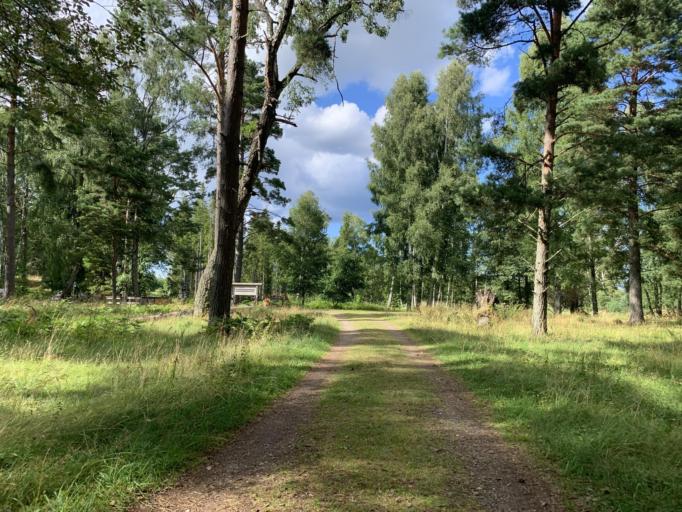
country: SE
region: Stockholm
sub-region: Sodertalje Kommun
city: Pershagen
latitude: 59.1035
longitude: 17.6806
